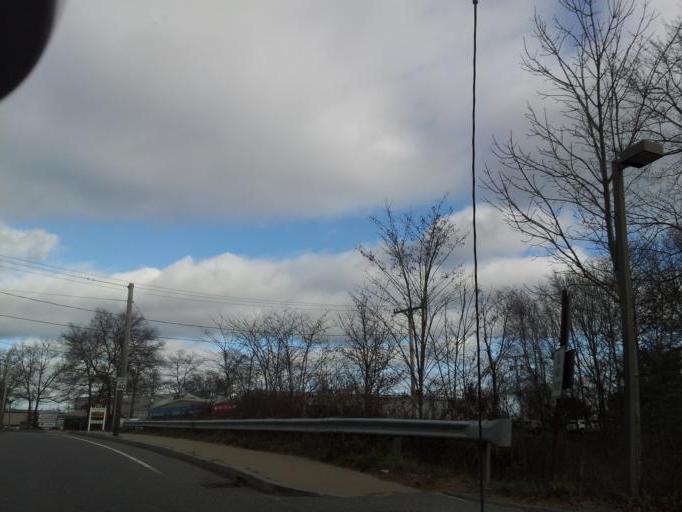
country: US
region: Massachusetts
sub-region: Plymouth County
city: Plymouth
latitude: 41.9267
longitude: -70.6562
